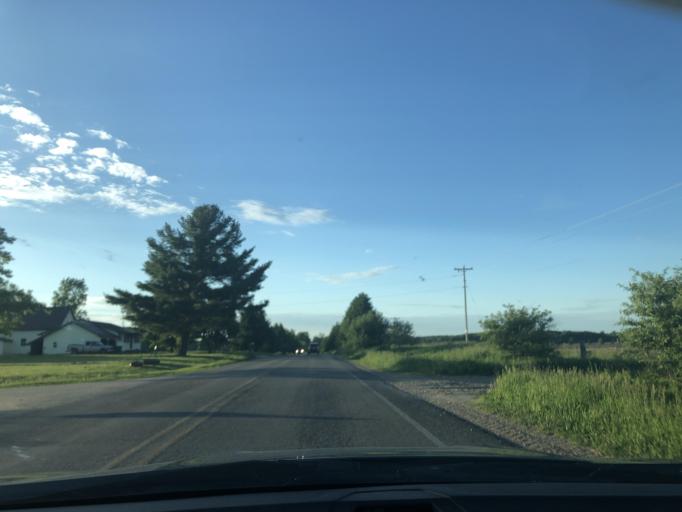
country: US
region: Michigan
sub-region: Missaukee County
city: Lake City
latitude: 44.4297
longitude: -85.0751
